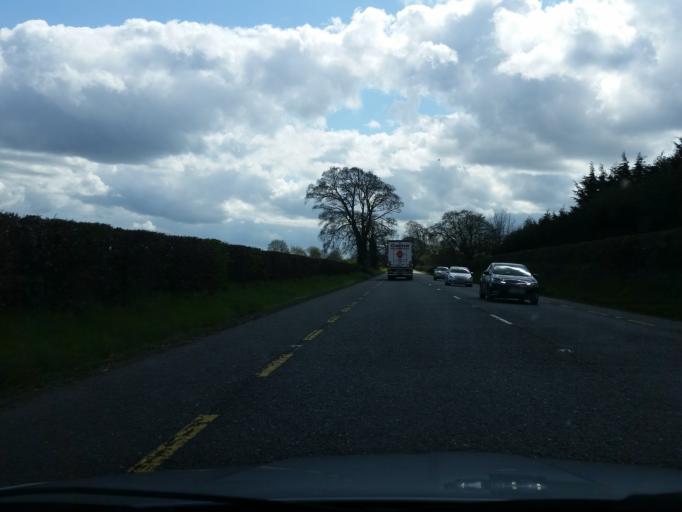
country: IE
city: Kentstown
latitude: 53.6097
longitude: -6.4766
